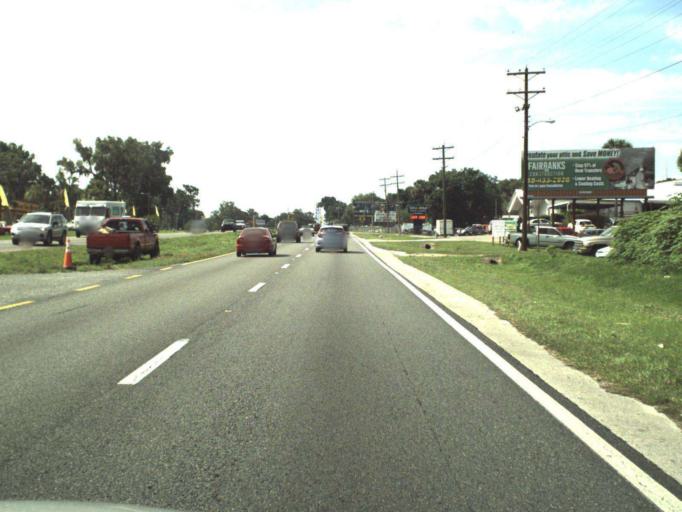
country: US
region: Florida
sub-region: Marion County
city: Ocala
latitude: 29.1441
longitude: -82.1128
